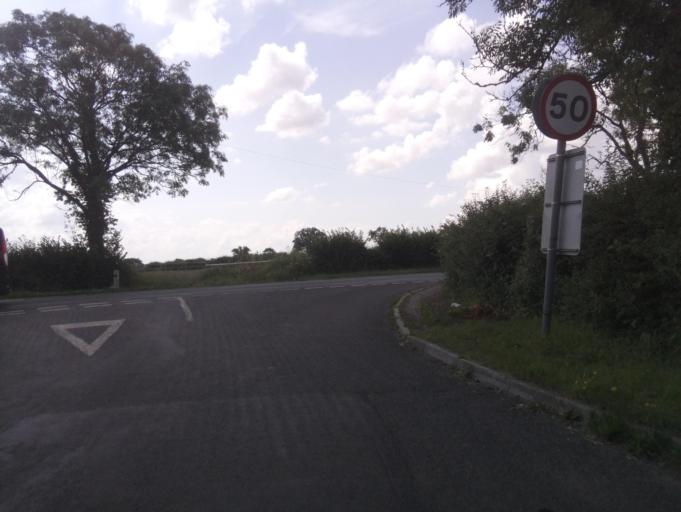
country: GB
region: England
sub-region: Wiltshire
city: Charlton
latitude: 51.5646
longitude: -2.0364
